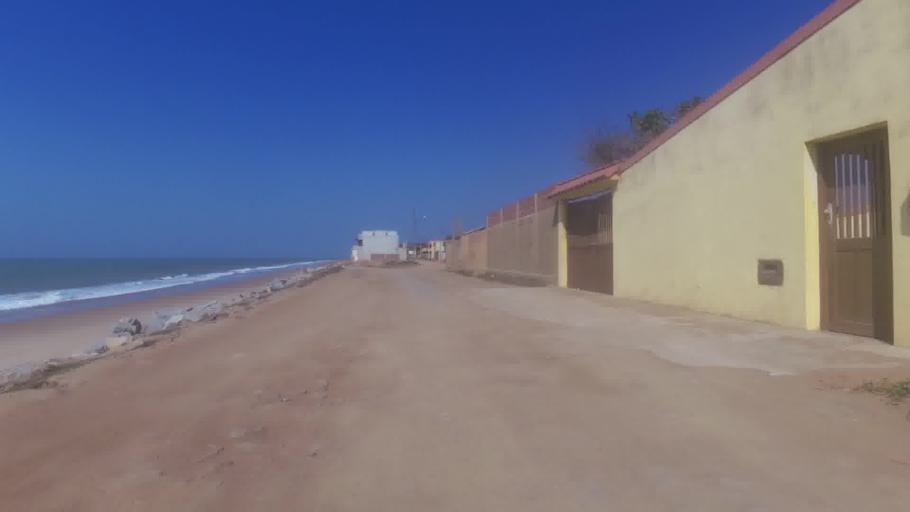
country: BR
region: Espirito Santo
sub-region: Marataizes
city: Marataizes
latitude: -21.0646
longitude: -40.8356
